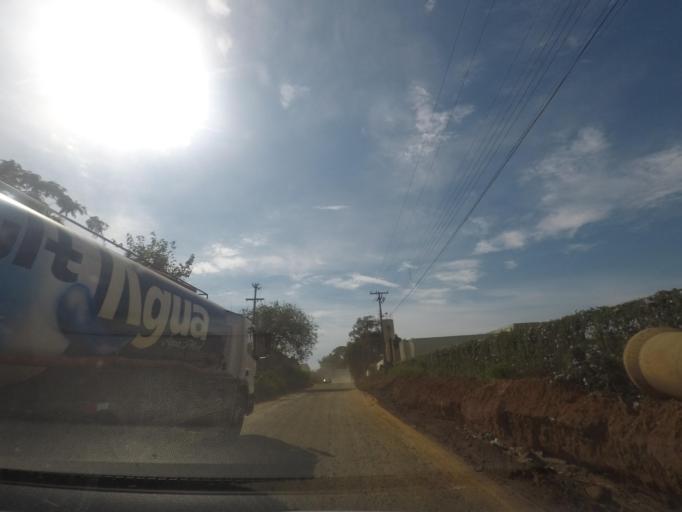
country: BR
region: Sao Paulo
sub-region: Sumare
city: Sumare
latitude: -22.7920
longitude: -47.2311
